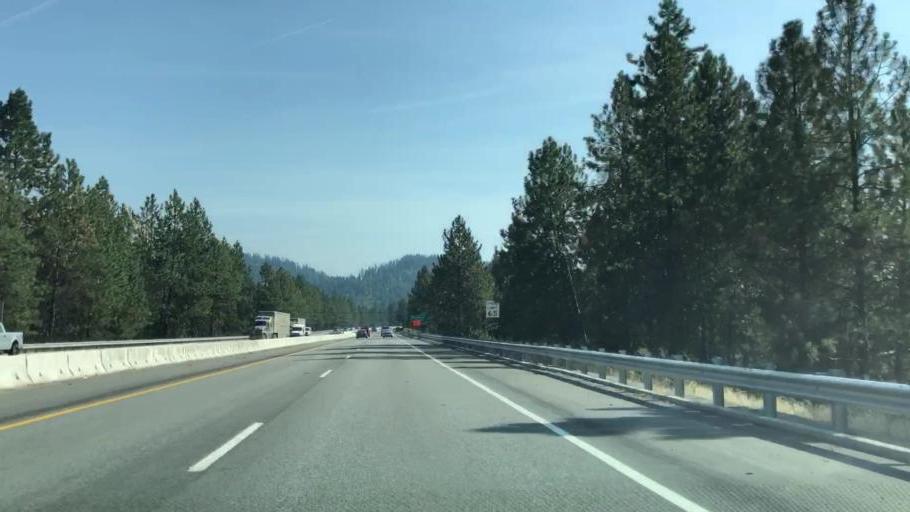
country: US
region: Idaho
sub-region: Kootenai County
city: Coeur d'Alene
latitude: 47.6807
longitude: -116.7572
